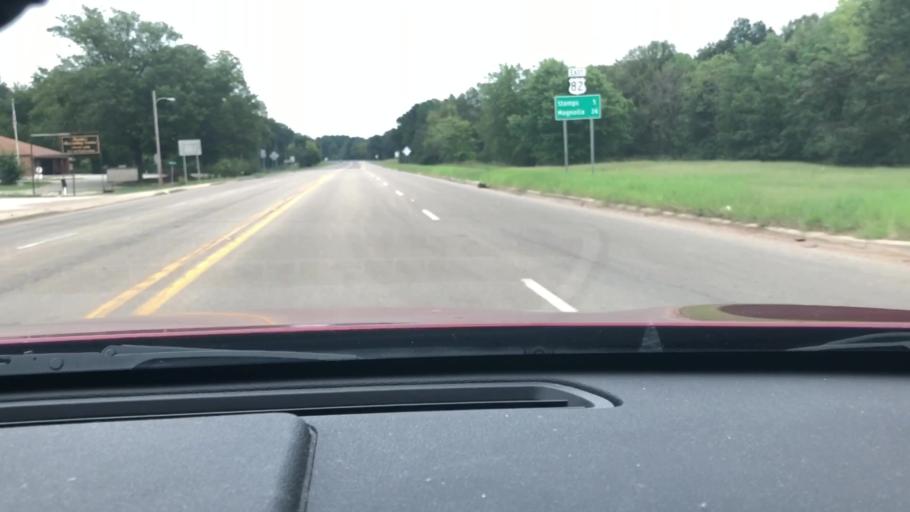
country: US
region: Arkansas
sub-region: Lafayette County
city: Lewisville
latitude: 33.3553
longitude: -93.5762
